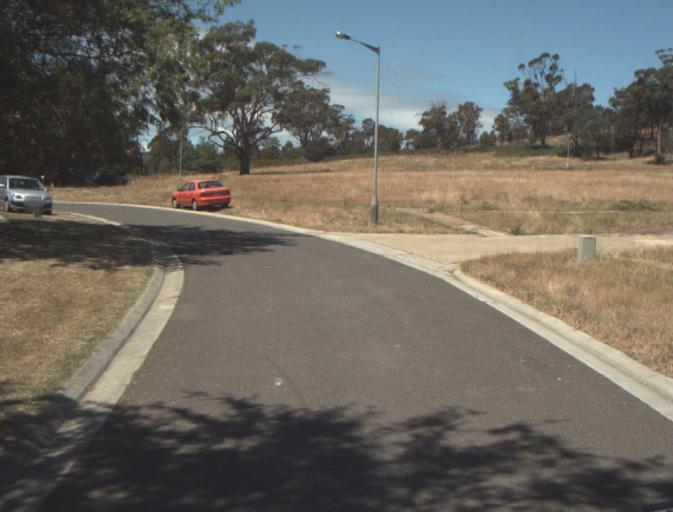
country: AU
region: Tasmania
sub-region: Launceston
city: Mayfield
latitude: -41.3757
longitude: 147.1398
